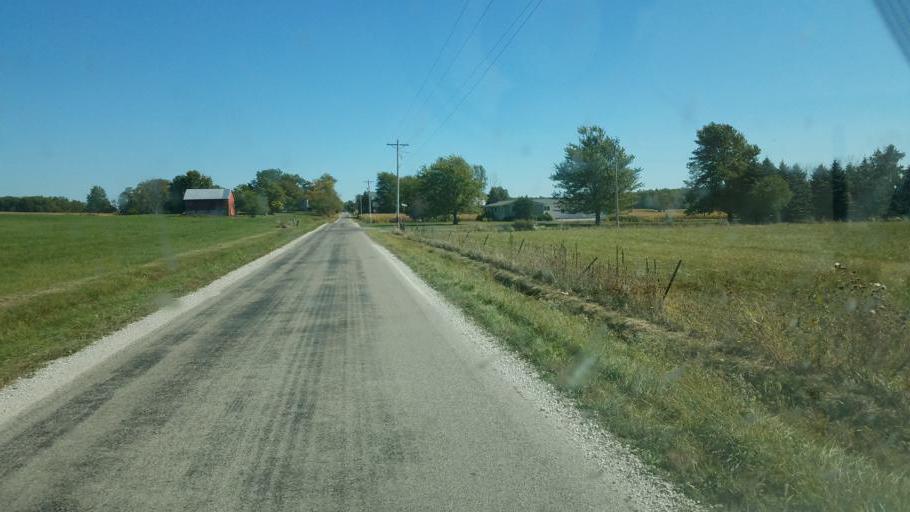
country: US
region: Ohio
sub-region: Huron County
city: Willard
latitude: 40.9458
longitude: -82.8267
